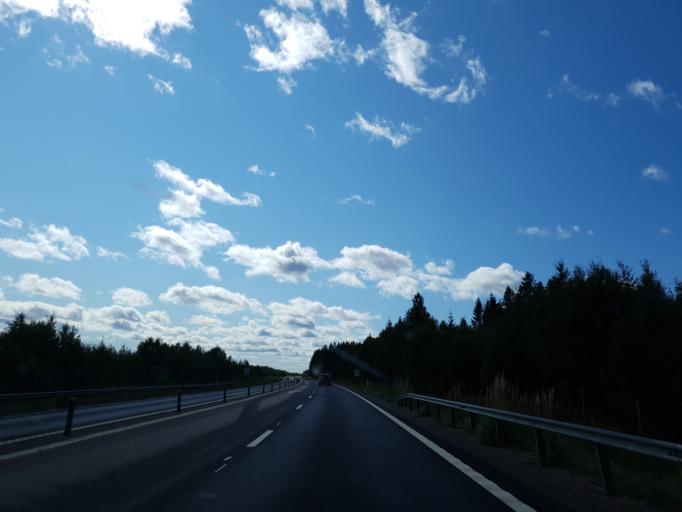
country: SE
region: Vaesterbotten
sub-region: Nordmalings Kommun
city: Nordmaling
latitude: 63.5660
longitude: 19.4315
